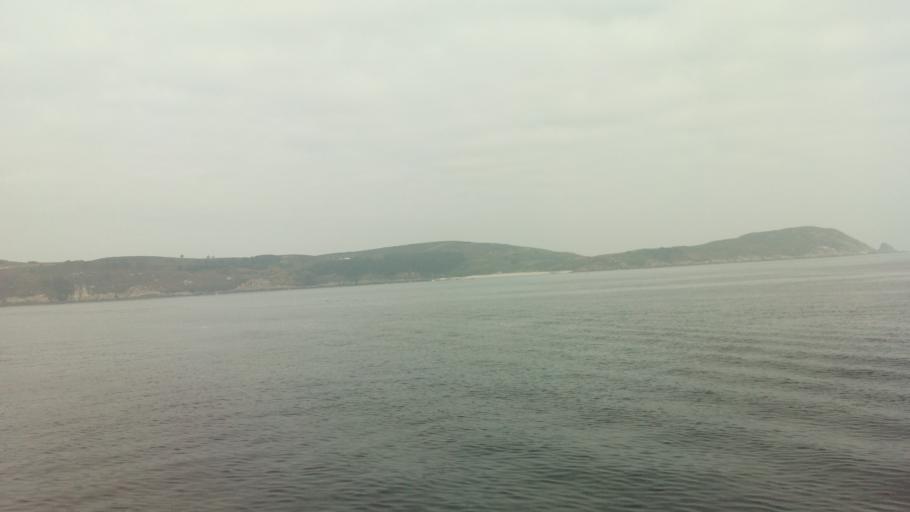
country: ES
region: Galicia
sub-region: Provincia de Pontevedra
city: Sanxenxo
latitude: 42.3789
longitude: -8.9110
